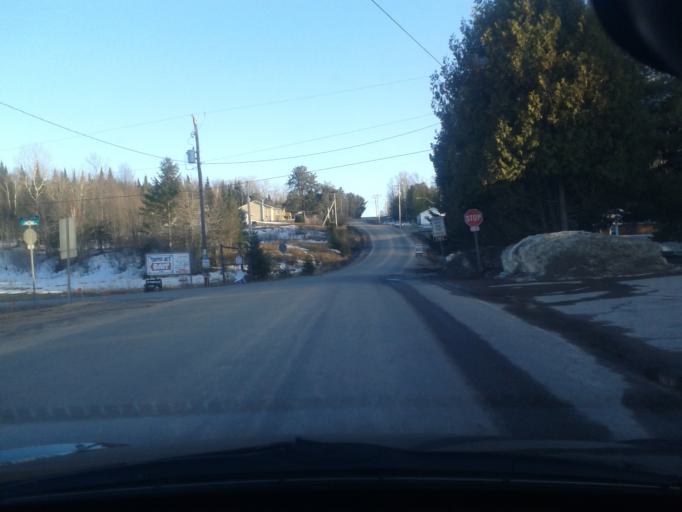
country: CA
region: Ontario
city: Powassan
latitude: 46.1842
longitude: -79.2778
